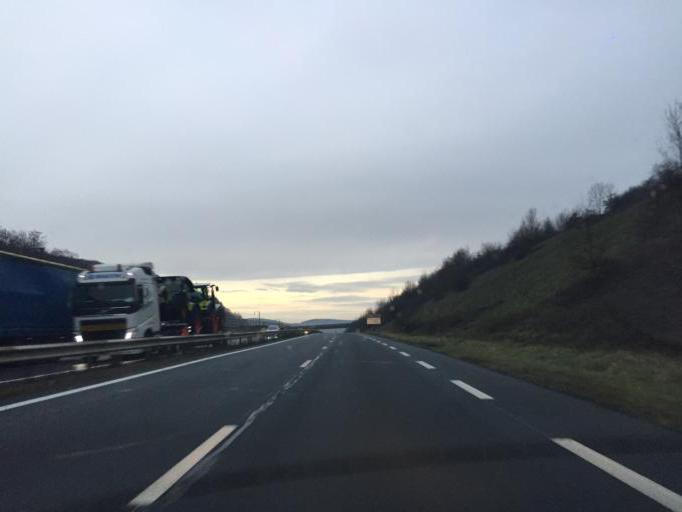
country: FR
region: Bourgogne
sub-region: Departement de Saone-et-Loire
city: Cluny
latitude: 46.3805
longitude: 4.6693
